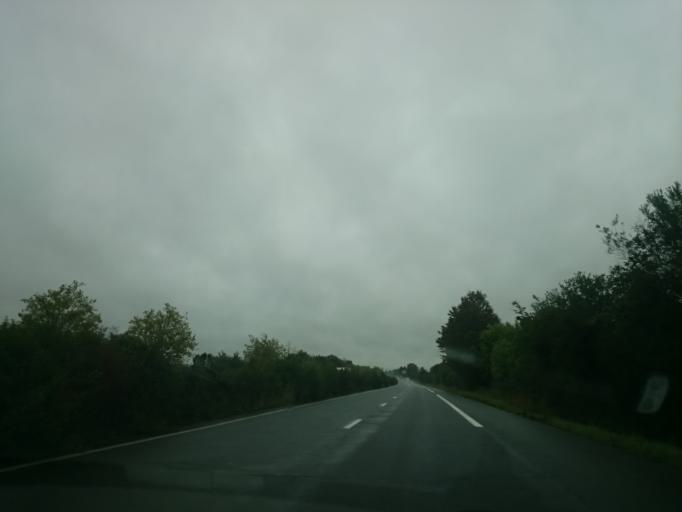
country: FR
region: Pays de la Loire
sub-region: Departement de la Loire-Atlantique
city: Missillac
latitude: 47.4579
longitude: -2.1441
